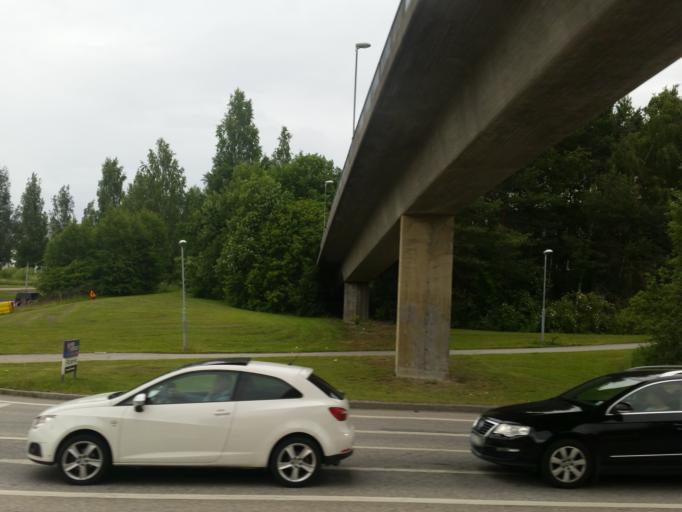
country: SE
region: Stockholm
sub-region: Stockholms Kommun
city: Kista
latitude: 59.4189
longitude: 17.9165
